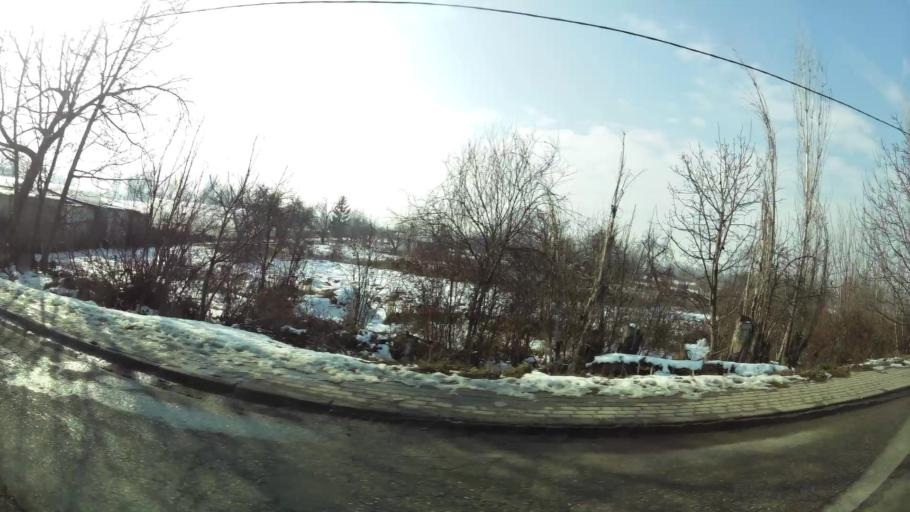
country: MK
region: Suto Orizari
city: Suto Orizare
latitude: 42.0237
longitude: 21.3852
